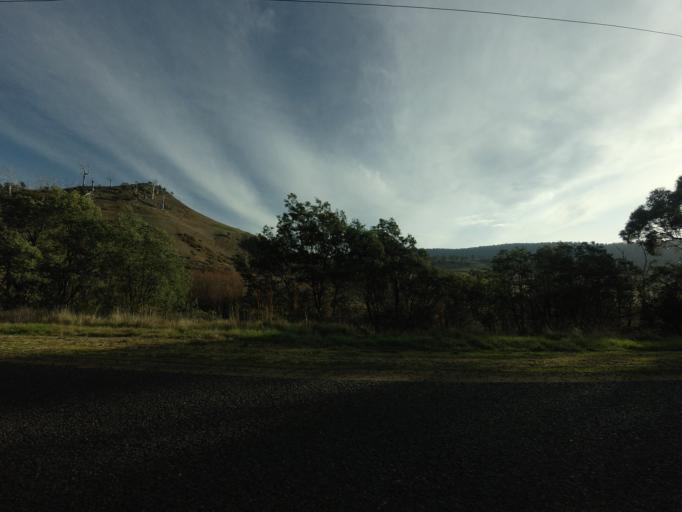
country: AU
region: Tasmania
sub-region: Brighton
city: Bridgewater
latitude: -42.4439
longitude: 147.1520
